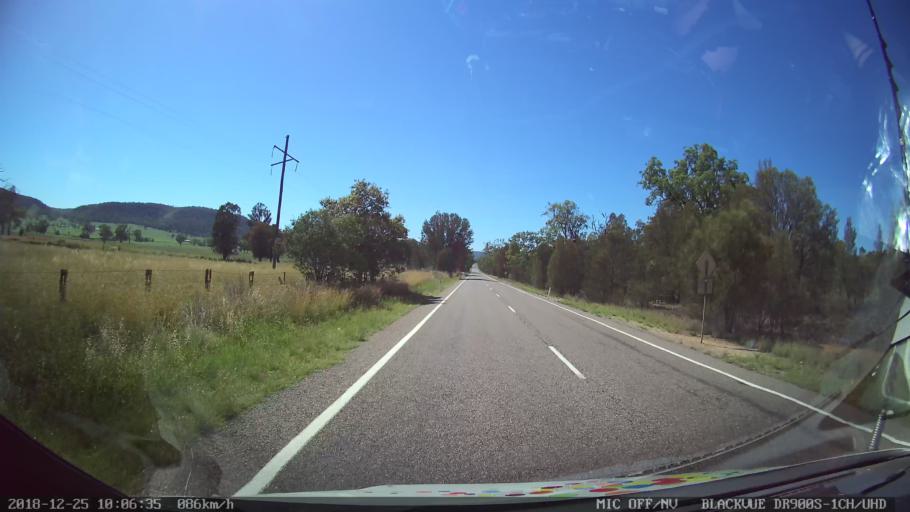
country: AU
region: New South Wales
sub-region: Upper Hunter Shire
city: Merriwa
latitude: -32.2616
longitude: 150.4907
